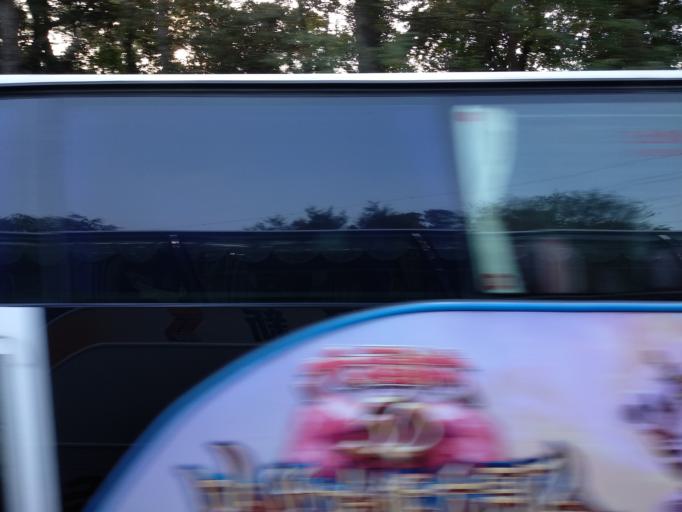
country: TW
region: Taiwan
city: Daxi
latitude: 24.8245
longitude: 121.1828
